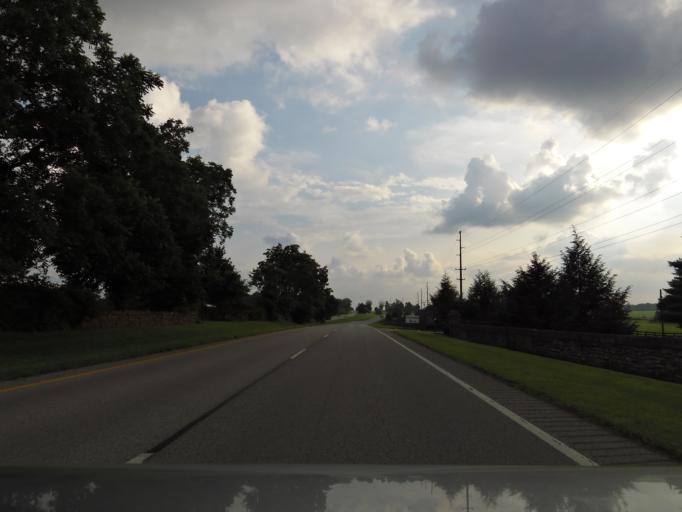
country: US
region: Kentucky
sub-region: Fayette County
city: Lexington-Fayette
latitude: 38.1213
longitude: -84.3869
